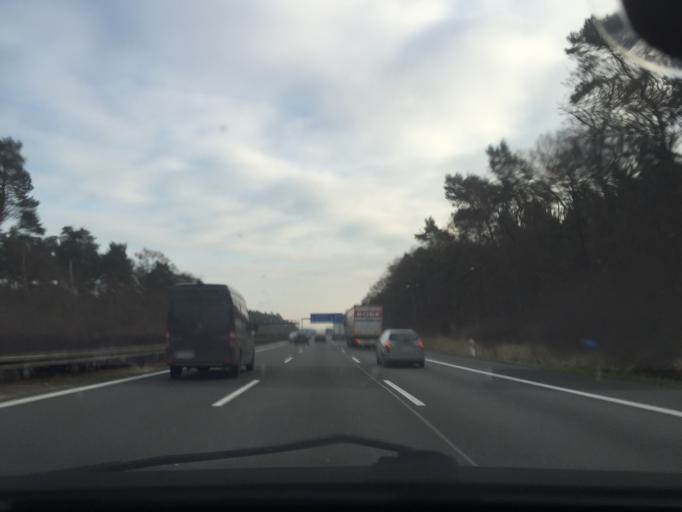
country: DE
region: Brandenburg
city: Fichtenwalde
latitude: 52.3147
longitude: 12.8670
